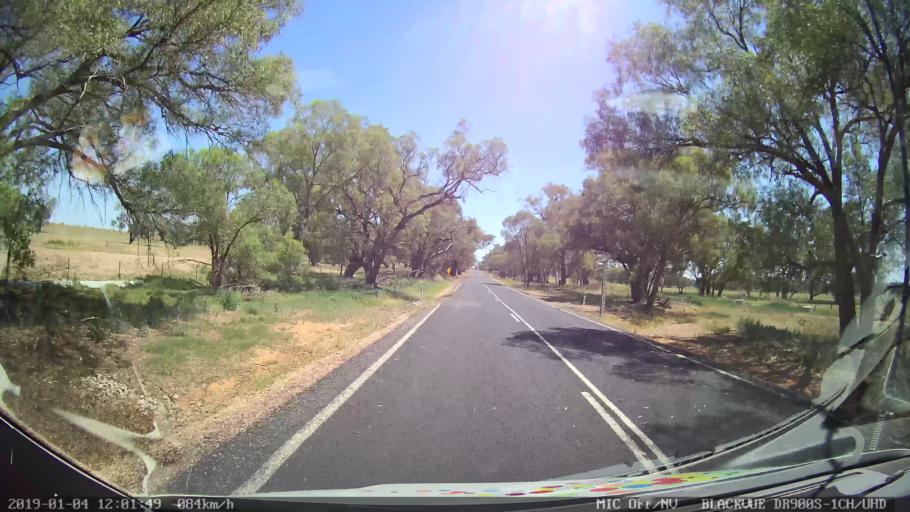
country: AU
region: New South Wales
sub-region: Wellington
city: Wellington
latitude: -32.7861
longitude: 148.6884
